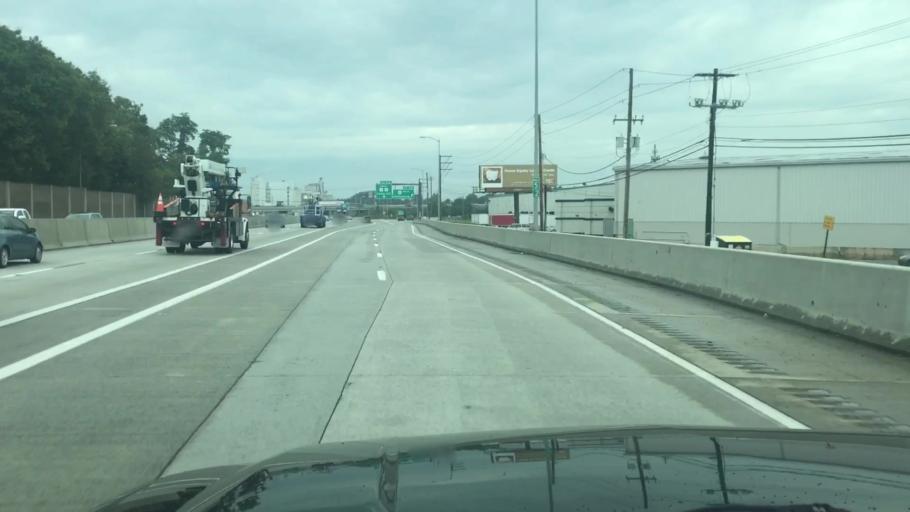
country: US
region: Pennsylvania
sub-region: Cumberland County
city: Shiremanstown
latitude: 40.2318
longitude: -76.9390
